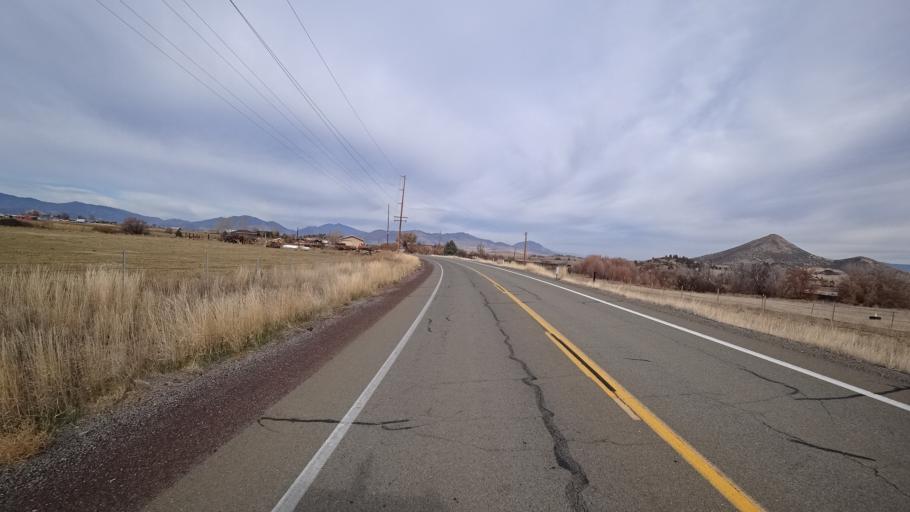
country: US
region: California
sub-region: Siskiyou County
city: Montague
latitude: 41.6969
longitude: -122.5352
